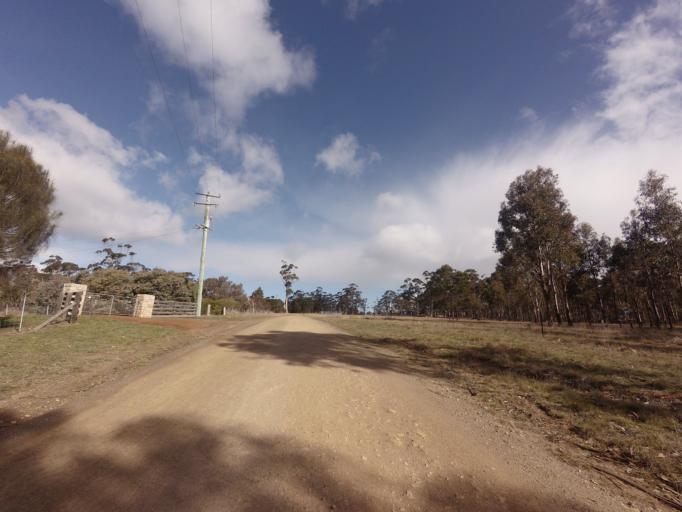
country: AU
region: Tasmania
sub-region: Sorell
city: Sorell
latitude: -42.3276
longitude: 147.9682
